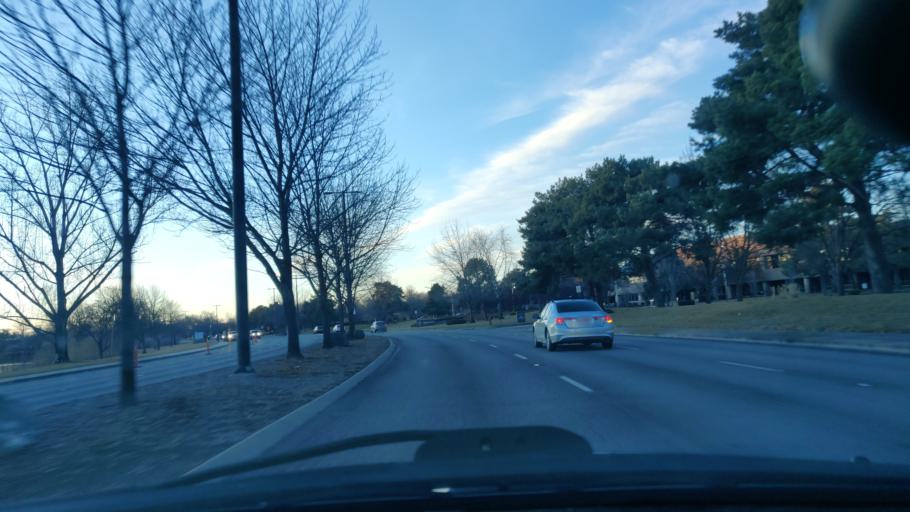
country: US
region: Idaho
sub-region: Ada County
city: Boise
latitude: 43.5981
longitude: -116.1793
